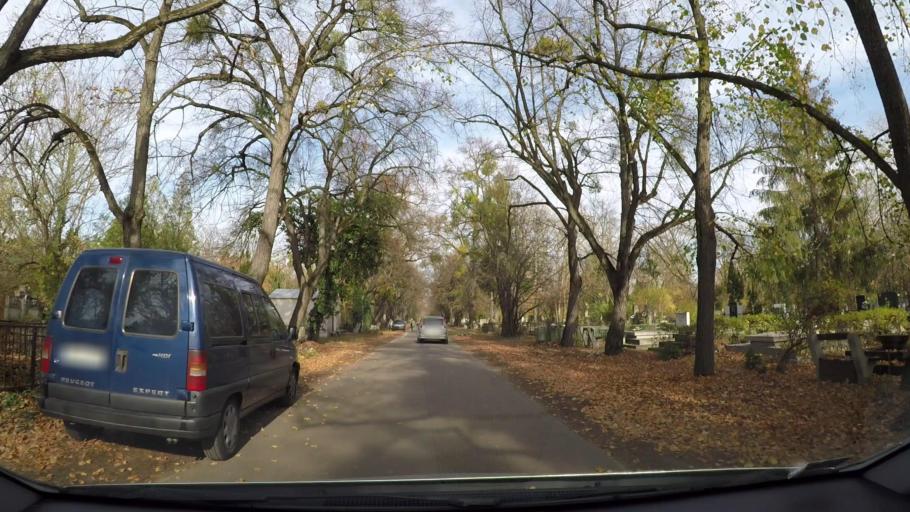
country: HU
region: Budapest
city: Budapest X. keruelet
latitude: 47.4732
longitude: 19.1847
